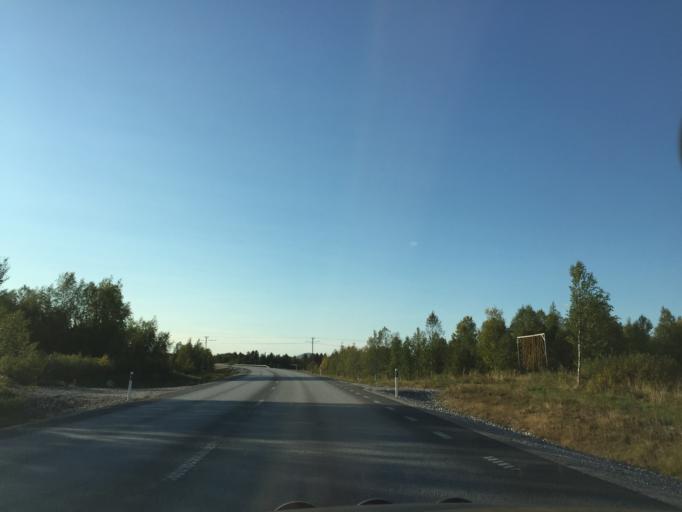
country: SE
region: Norrbotten
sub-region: Gallivare Kommun
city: Malmberget
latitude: 67.6430
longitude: 21.0539
